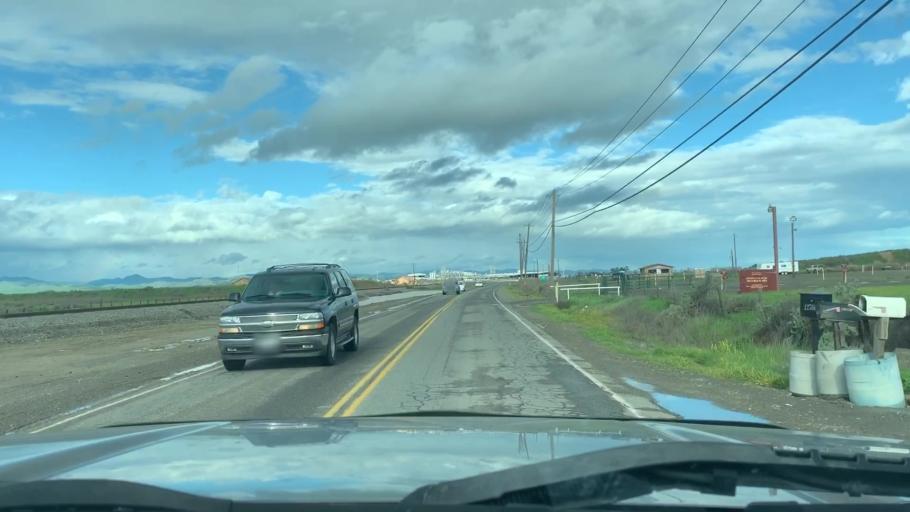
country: US
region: California
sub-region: Merced County
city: Los Banos
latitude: 37.1034
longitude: -120.9343
